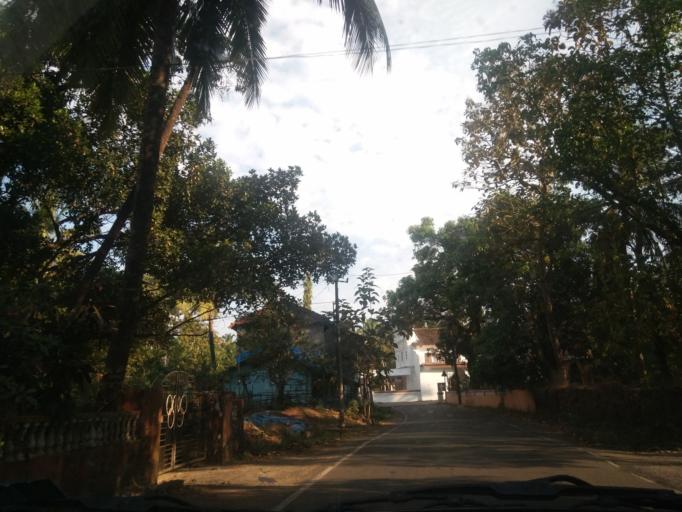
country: IN
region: Goa
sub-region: South Goa
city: Varca
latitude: 15.2426
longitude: 73.9563
